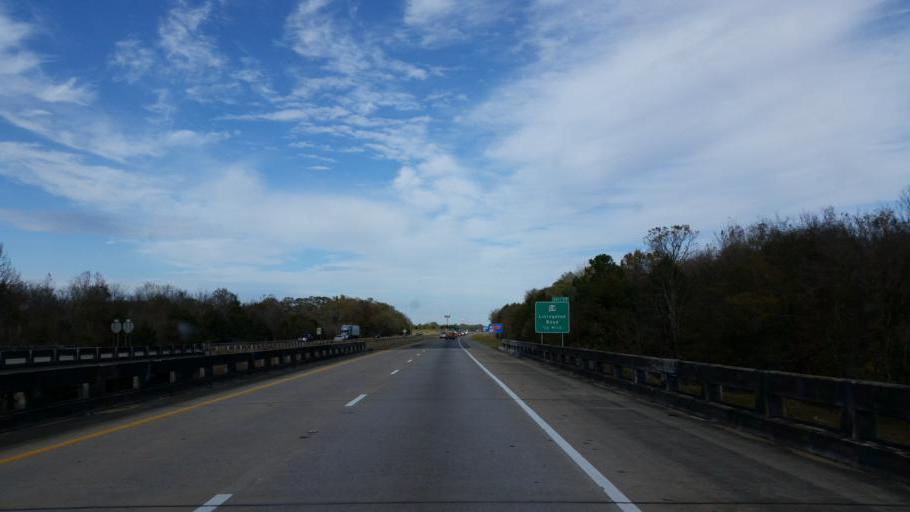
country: US
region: Alabama
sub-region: Sumter County
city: Livingston
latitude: 32.6161
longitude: -88.2135
